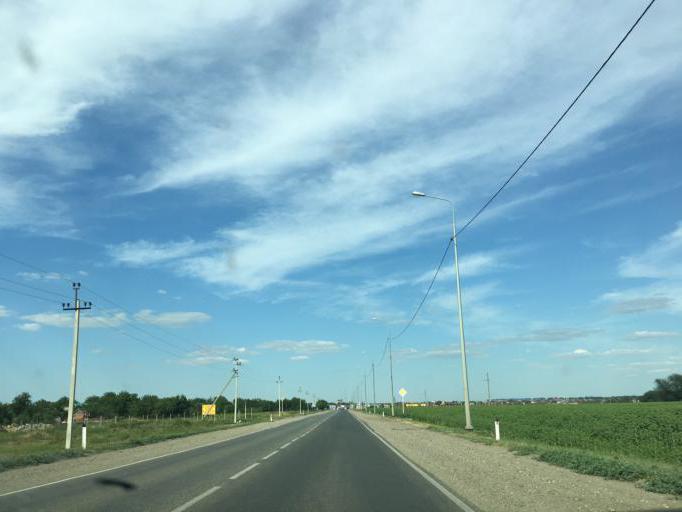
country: RU
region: Krasnodarskiy
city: Kushchevskaya
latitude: 46.5460
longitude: 39.6376
